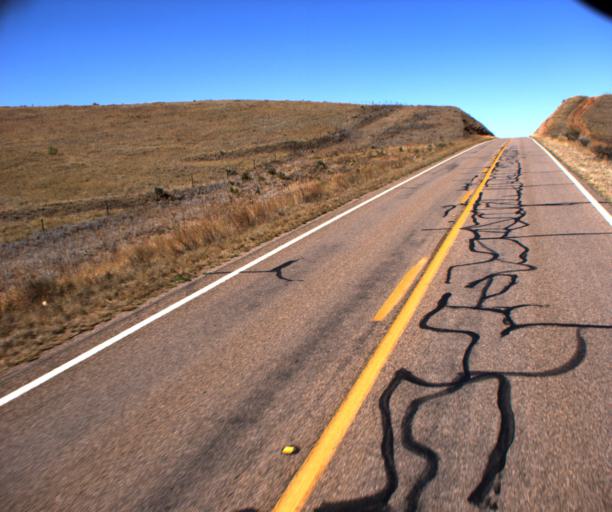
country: US
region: Arizona
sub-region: Cochise County
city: Huachuca City
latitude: 31.7077
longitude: -110.5790
